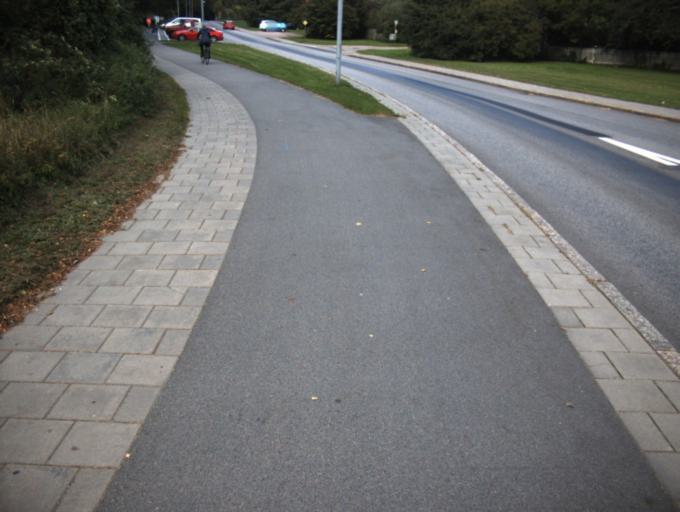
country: SE
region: Skane
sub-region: Helsingborg
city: Helsingborg
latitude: 56.0636
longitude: 12.6936
